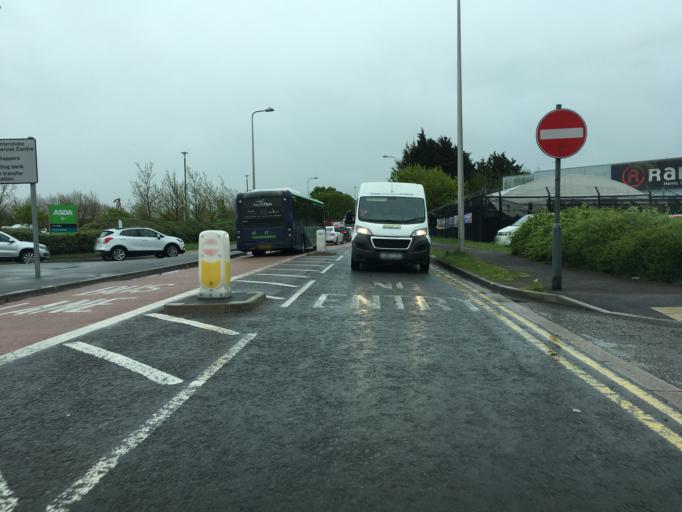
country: GB
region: England
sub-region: North Somerset
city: Weston-super-Mare
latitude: 51.3399
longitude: -2.9599
